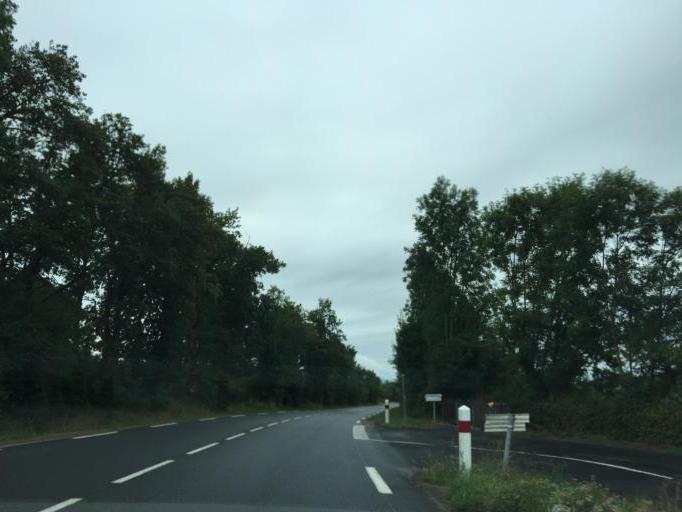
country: FR
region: Midi-Pyrenees
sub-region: Departement de l'Aveyron
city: Espalion
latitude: 44.5758
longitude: 2.7960
